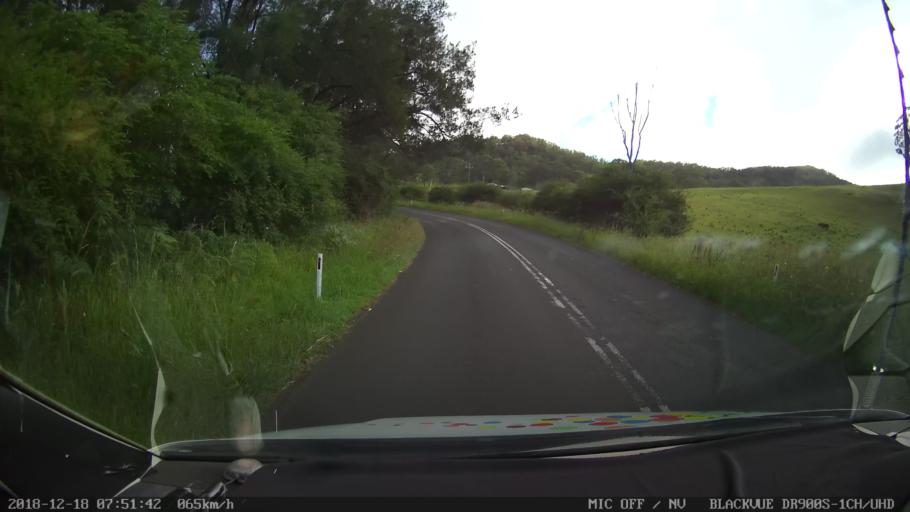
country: AU
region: New South Wales
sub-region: Kyogle
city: Kyogle
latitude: -28.4357
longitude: 152.5803
